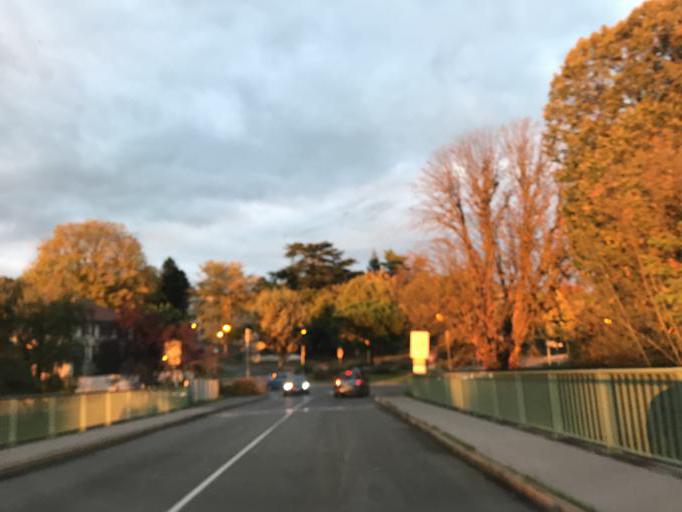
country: FR
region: Rhone-Alpes
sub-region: Departement de l'Ain
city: Trevoux
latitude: 45.9381
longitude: 4.7794
